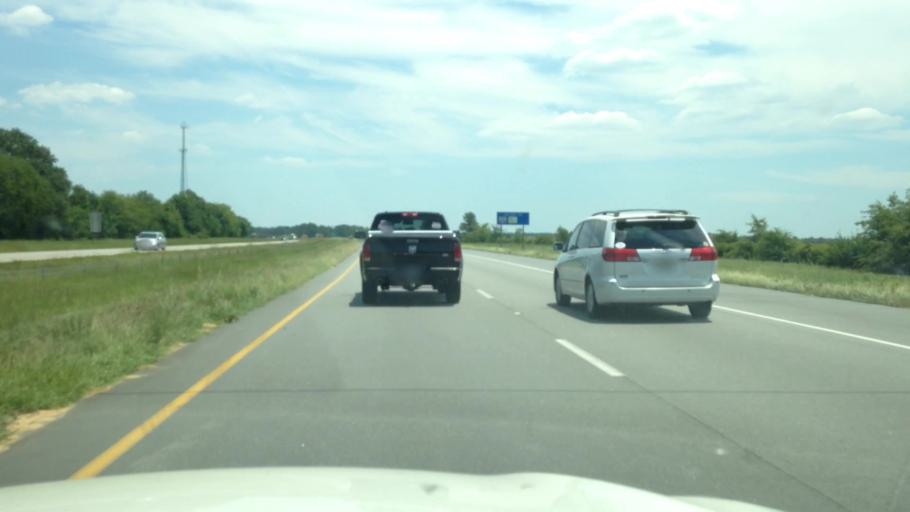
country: US
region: South Carolina
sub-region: Lee County
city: Bishopville
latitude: 34.1865
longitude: -80.2266
